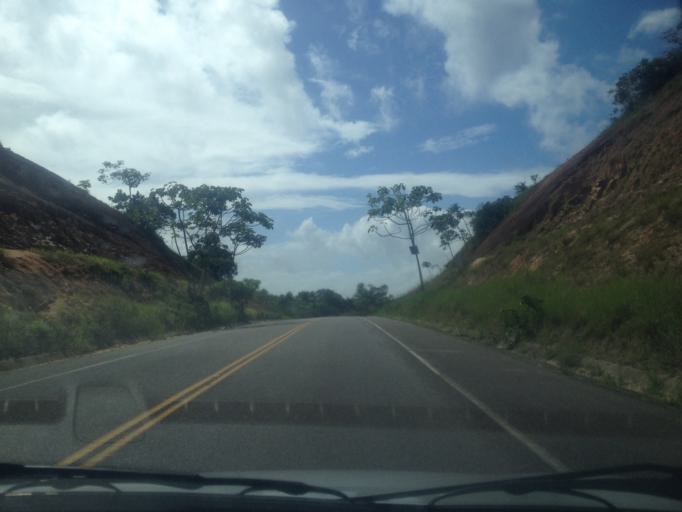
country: BR
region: Bahia
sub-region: Conde
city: Conde
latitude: -11.7791
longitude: -37.6130
